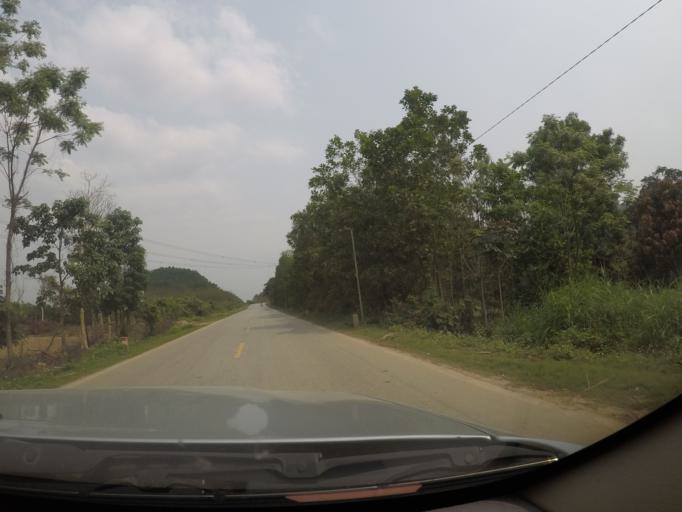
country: VN
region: Thanh Hoa
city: Thi Tran Yen Cat
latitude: 19.4770
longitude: 105.4142
